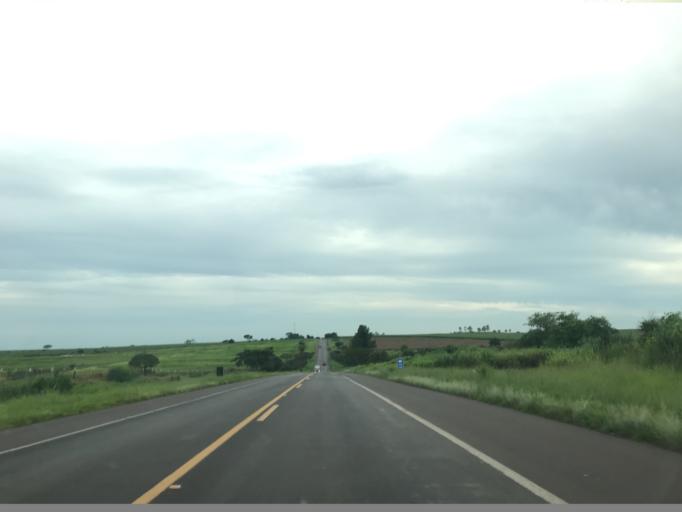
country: BR
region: Sao Paulo
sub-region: Tupa
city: Tupa
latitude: -21.6624
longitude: -50.5528
